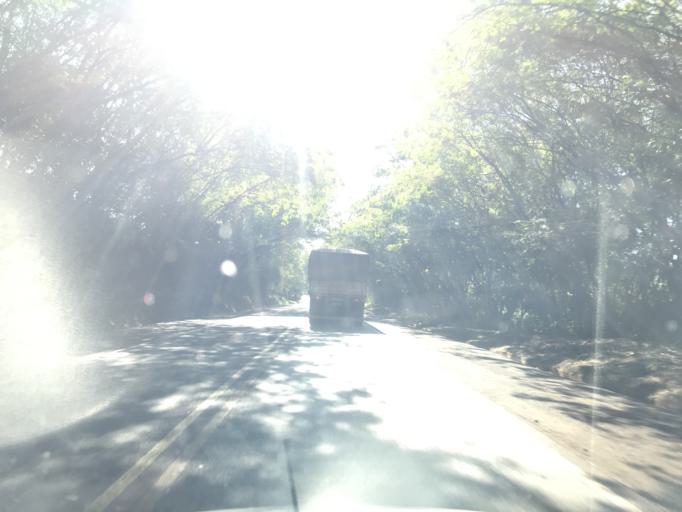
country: BR
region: Parana
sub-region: Umuarama
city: Umuarama
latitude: -23.8834
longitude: -53.3984
